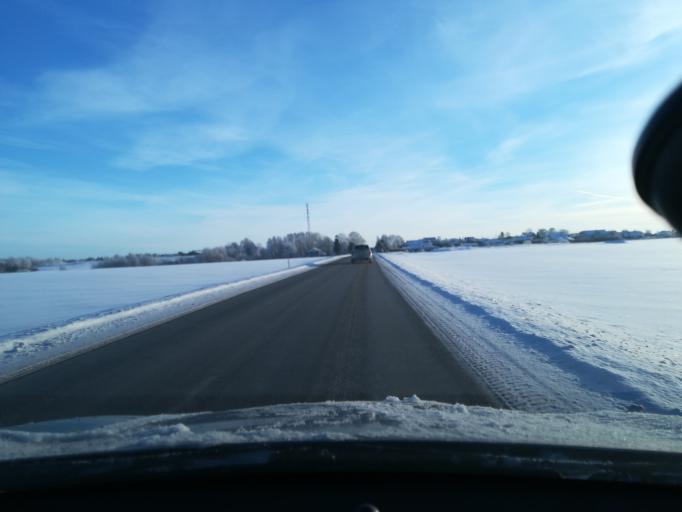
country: EE
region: Harju
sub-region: Harku vald
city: Tabasalu
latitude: 59.3668
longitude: 24.4824
